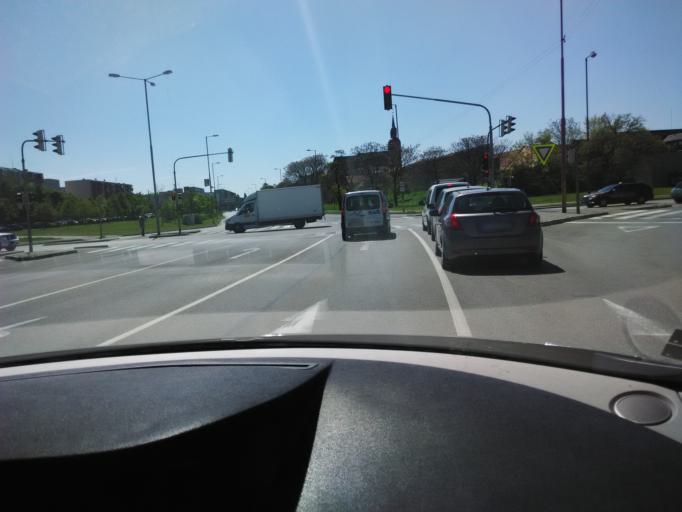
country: SK
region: Trnavsky
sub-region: Okres Trnava
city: Trnava
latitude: 48.3834
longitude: 17.5912
